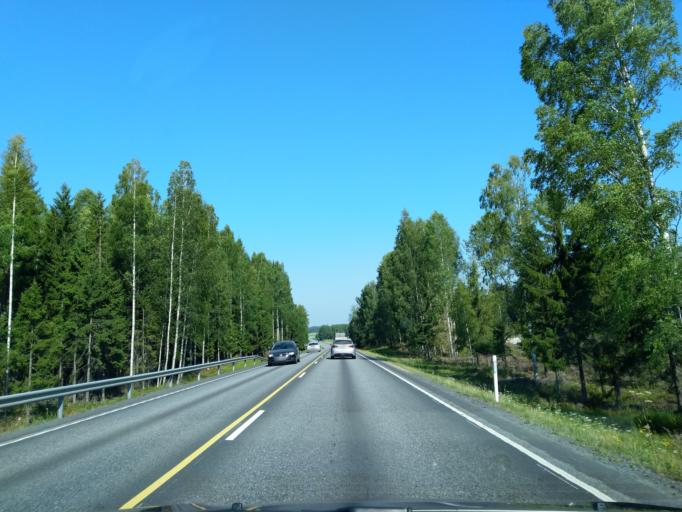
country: FI
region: Varsinais-Suomi
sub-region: Loimaa
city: Alastaro
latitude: 61.0813
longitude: 22.9018
